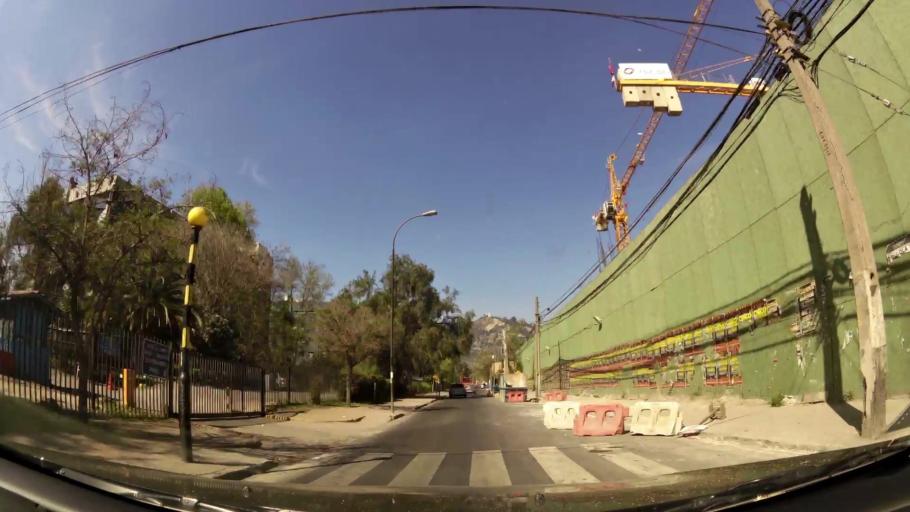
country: CL
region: Santiago Metropolitan
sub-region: Provincia de Santiago
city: Santiago
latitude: -33.4233
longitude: -70.6536
